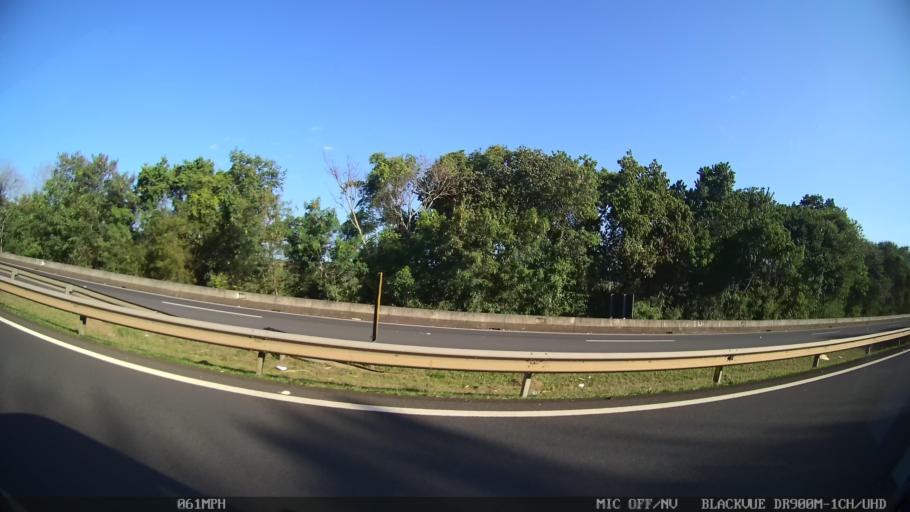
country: BR
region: Sao Paulo
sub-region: Piracicaba
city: Piracicaba
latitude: -22.6973
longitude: -47.6166
